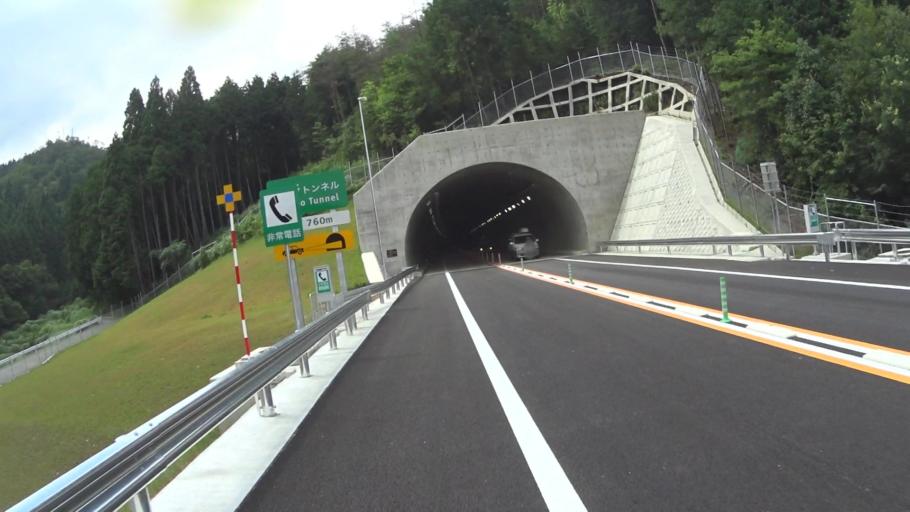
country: JP
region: Kyoto
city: Ayabe
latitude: 35.2039
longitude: 135.3505
